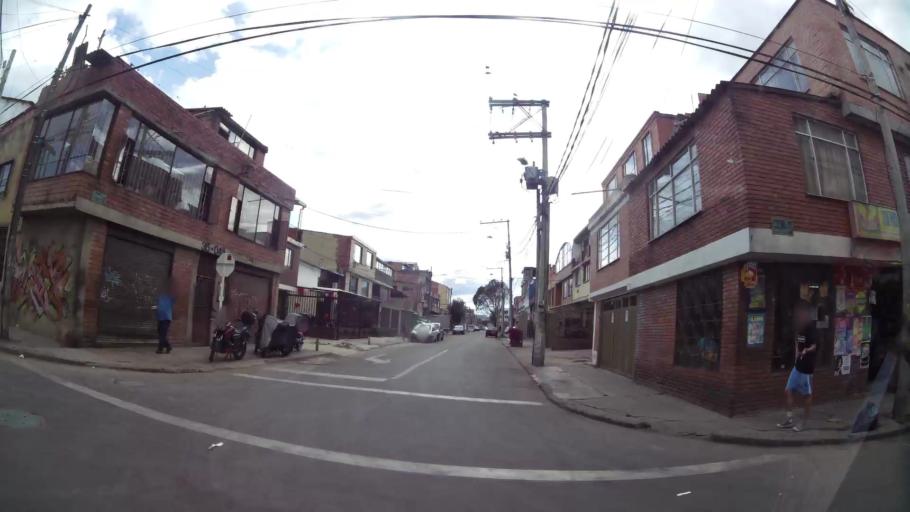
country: CO
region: Bogota D.C.
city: Bogota
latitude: 4.6115
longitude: -74.1378
